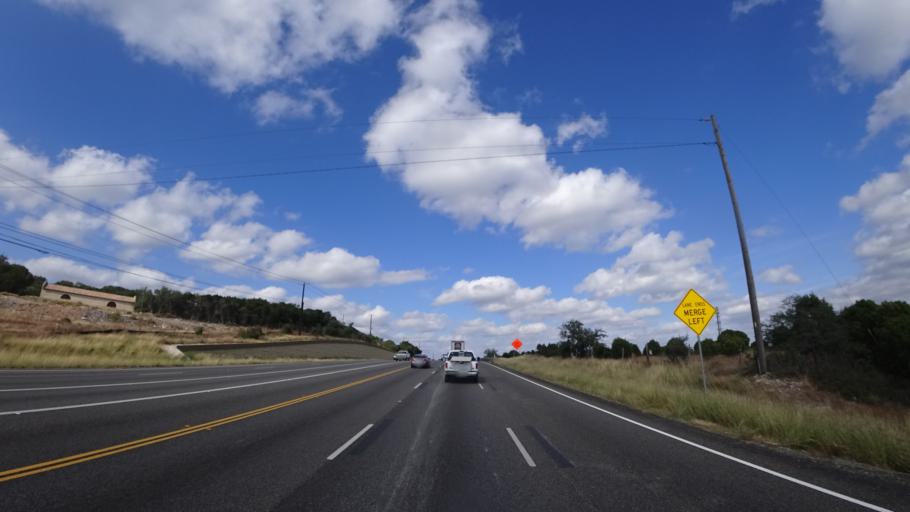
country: US
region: Texas
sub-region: Travis County
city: Bee Cave
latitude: 30.2769
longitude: -97.9149
